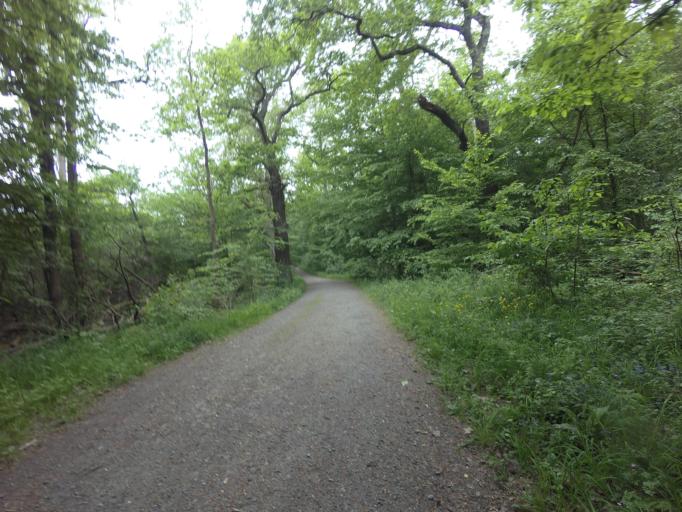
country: DE
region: Lower Saxony
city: Cremlingen
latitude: 52.2582
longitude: 10.5973
